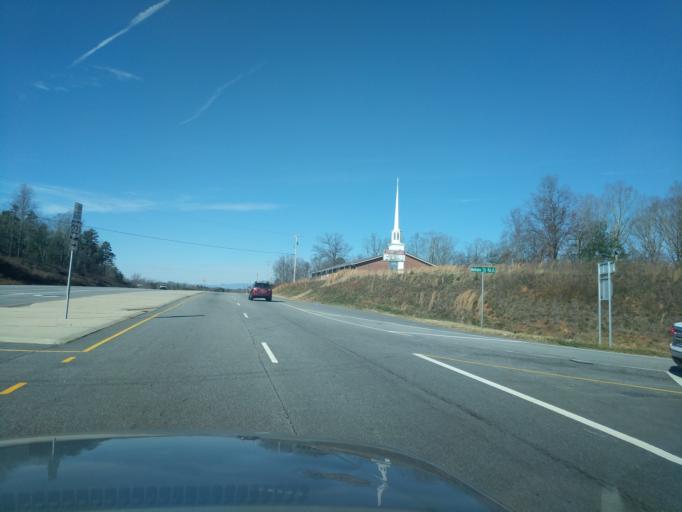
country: US
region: North Carolina
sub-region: Rutherford County
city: Forest City
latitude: 35.2963
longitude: -81.9121
